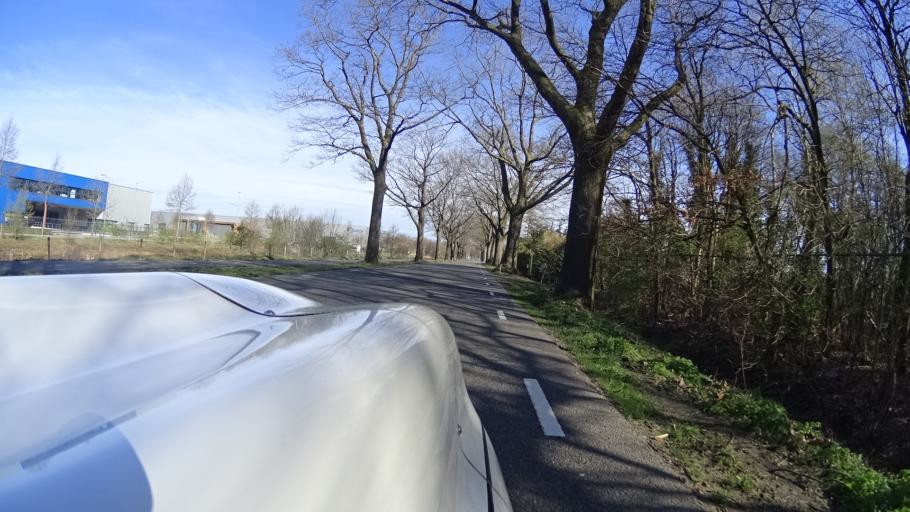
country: NL
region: North Brabant
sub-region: Gemeente Uden
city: Volkel
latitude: 51.6608
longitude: 5.6731
